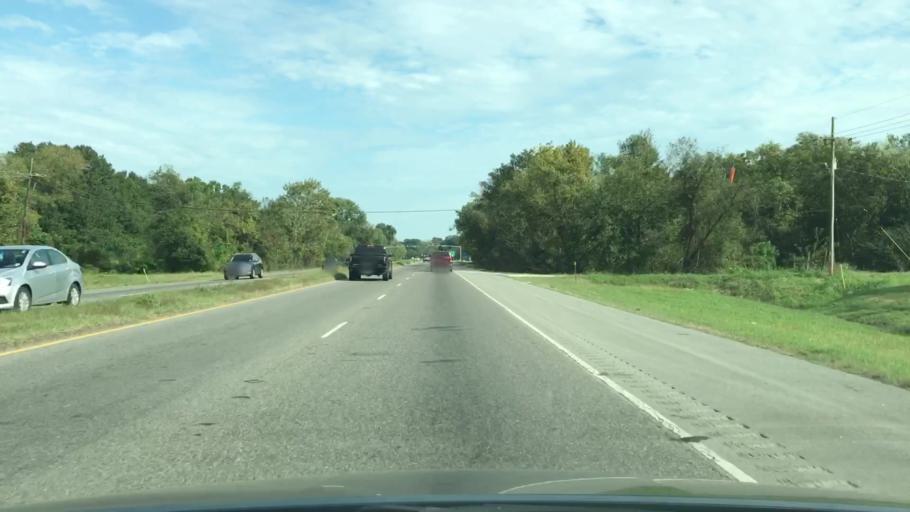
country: US
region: Louisiana
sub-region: Jefferson Parish
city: Avondale
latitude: 29.9094
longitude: -90.1951
